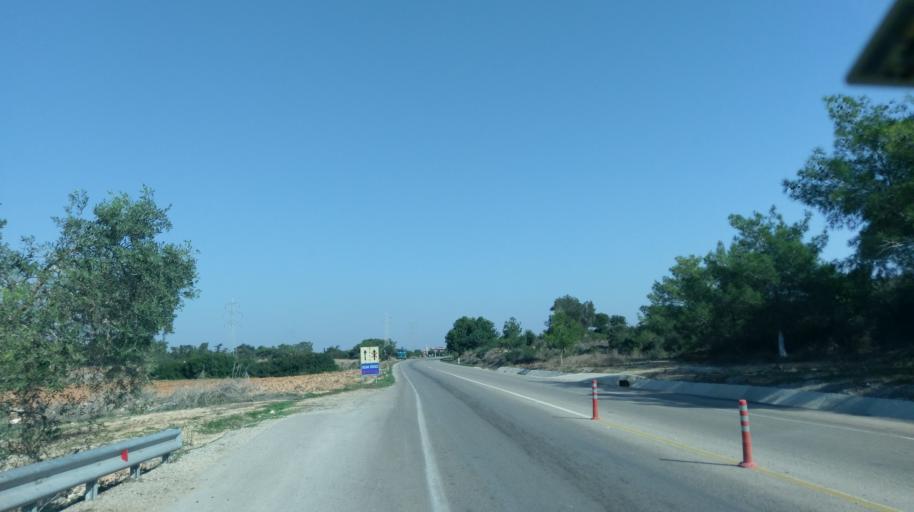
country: CY
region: Ammochostos
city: Leonarisso
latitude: 35.4810
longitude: 34.1443
